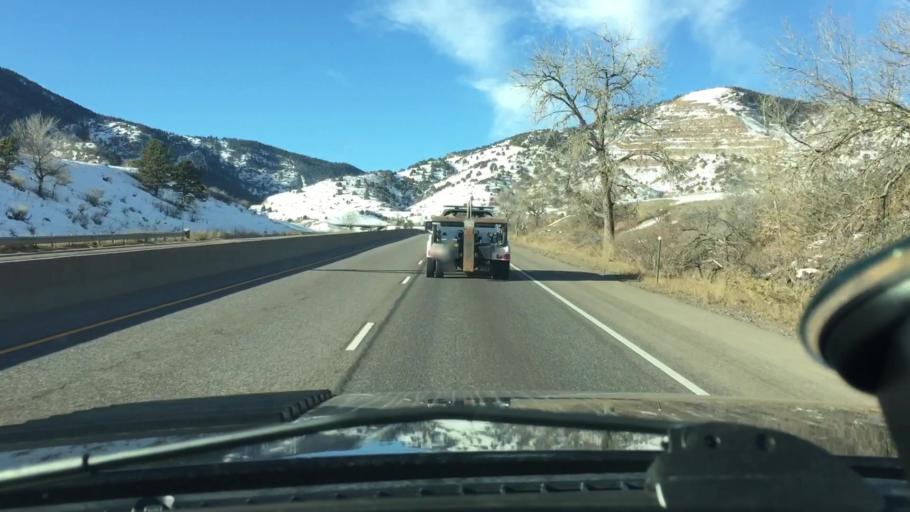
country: US
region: Colorado
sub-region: Jefferson County
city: Indian Hills
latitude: 39.6267
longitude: -105.1842
